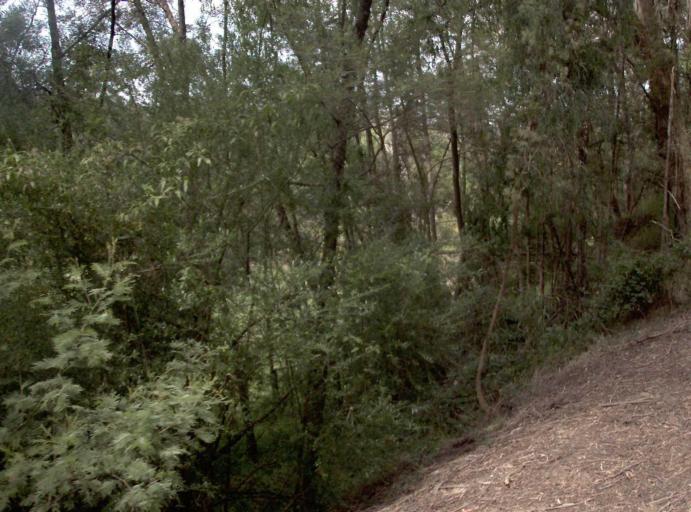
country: AU
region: New South Wales
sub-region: Bega Valley
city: Eden
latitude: -37.4783
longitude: 149.6158
